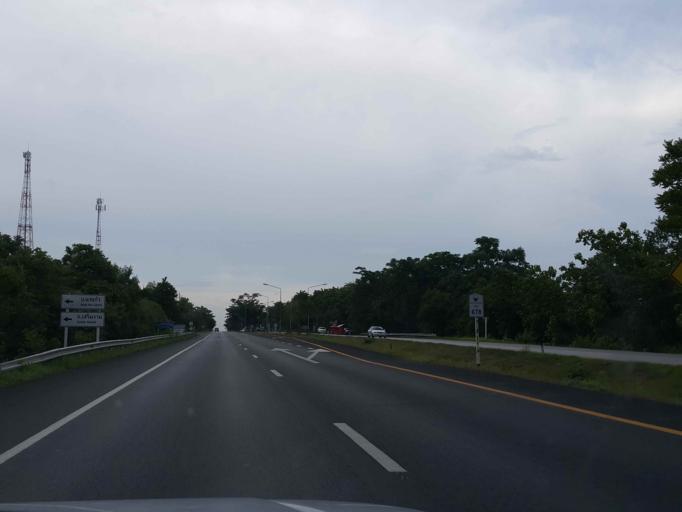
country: TH
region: Lampang
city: Ko Kha
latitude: 18.0910
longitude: 99.3964
